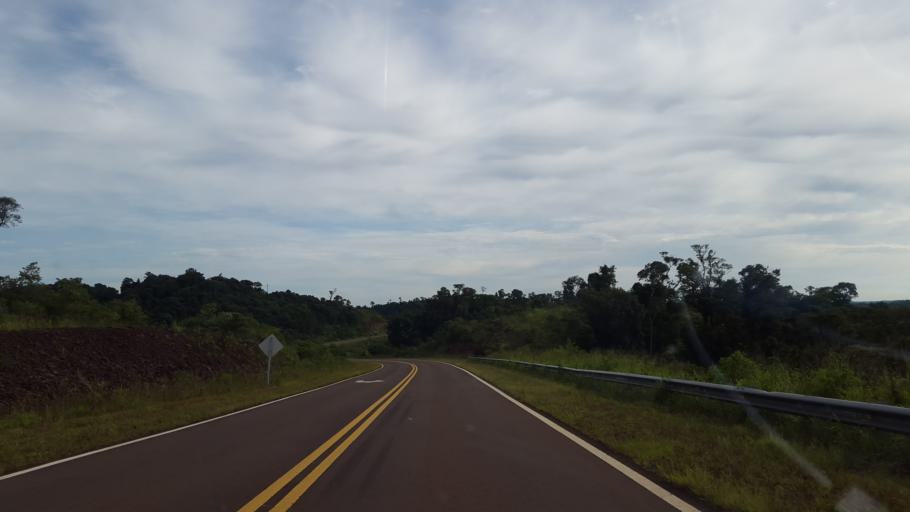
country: AR
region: Misiones
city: Bernardo de Irigoyen
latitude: -26.4078
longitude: -53.8225
